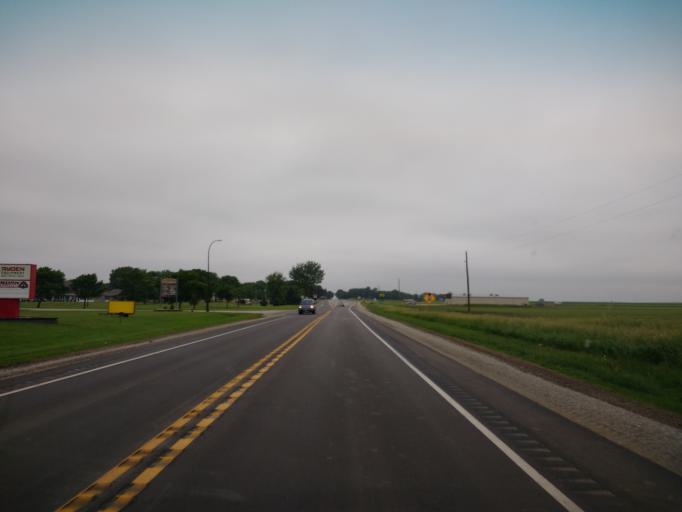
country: US
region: Iowa
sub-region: O'Brien County
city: Sanborn
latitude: 43.1861
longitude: -95.6390
